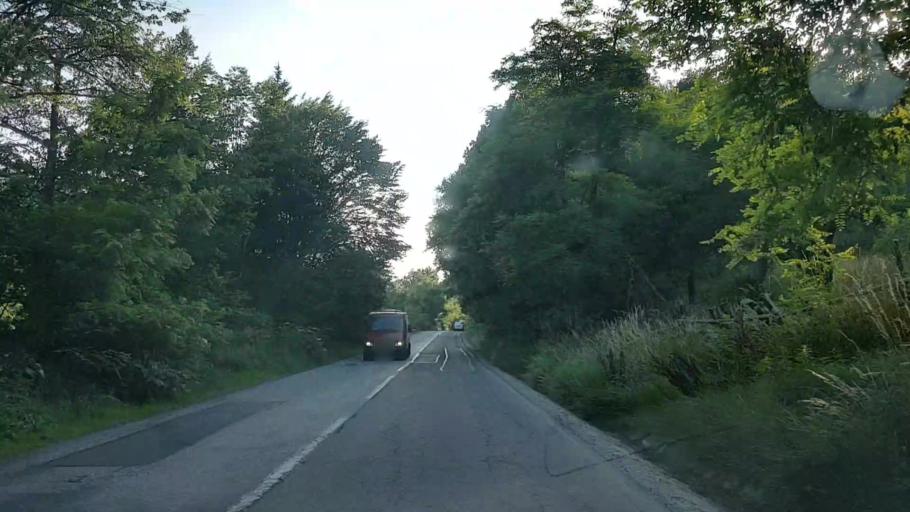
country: RO
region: Harghita
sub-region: Comuna Praid
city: Ocna de Sus
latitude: 46.5732
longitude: 25.2132
